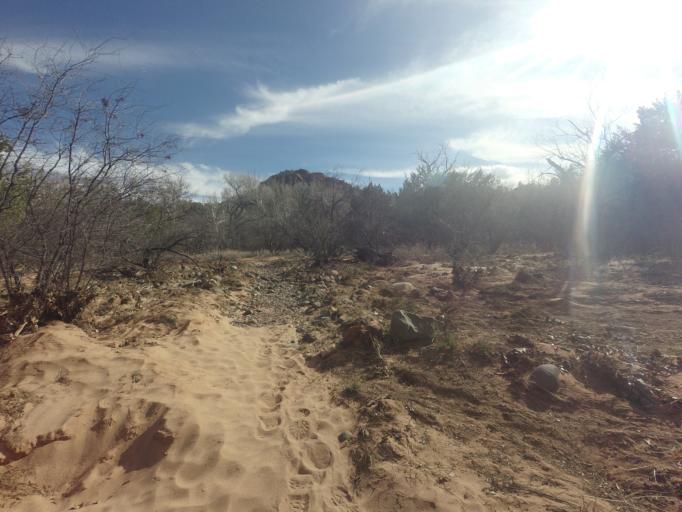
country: US
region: Arizona
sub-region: Yavapai County
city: West Sedona
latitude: 34.8092
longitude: -111.8287
